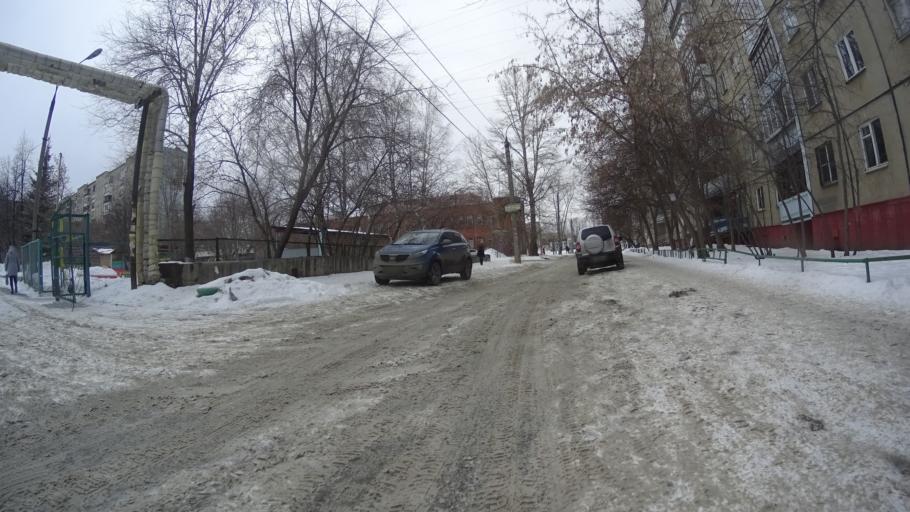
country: RU
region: Chelyabinsk
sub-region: Gorod Chelyabinsk
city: Chelyabinsk
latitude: 55.1775
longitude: 61.3369
